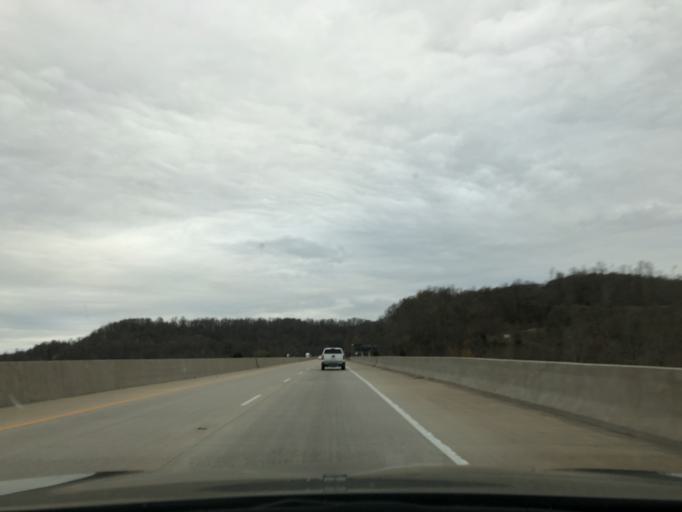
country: US
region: Arkansas
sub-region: Washington County
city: West Fork
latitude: 35.7796
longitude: -94.1864
